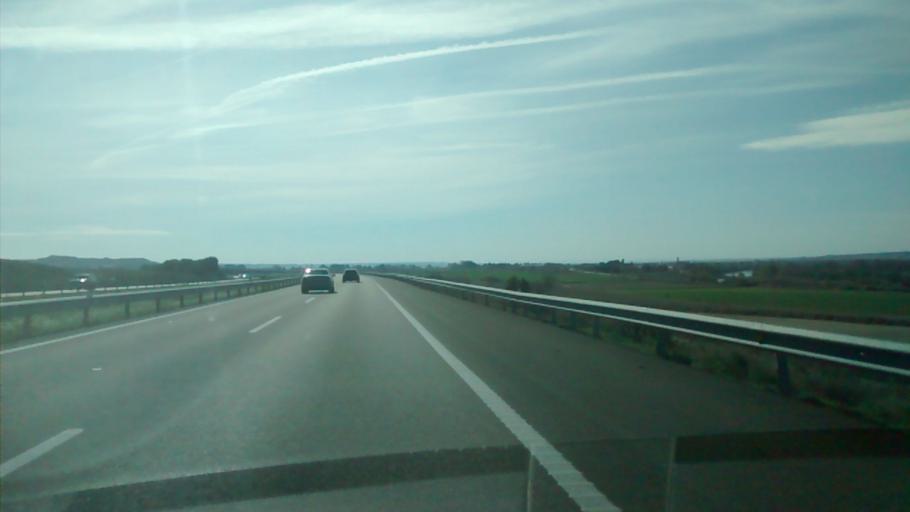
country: ES
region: Aragon
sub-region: Provincia de Zaragoza
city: Fuentes de Ebro
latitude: 41.5499
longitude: -0.5922
